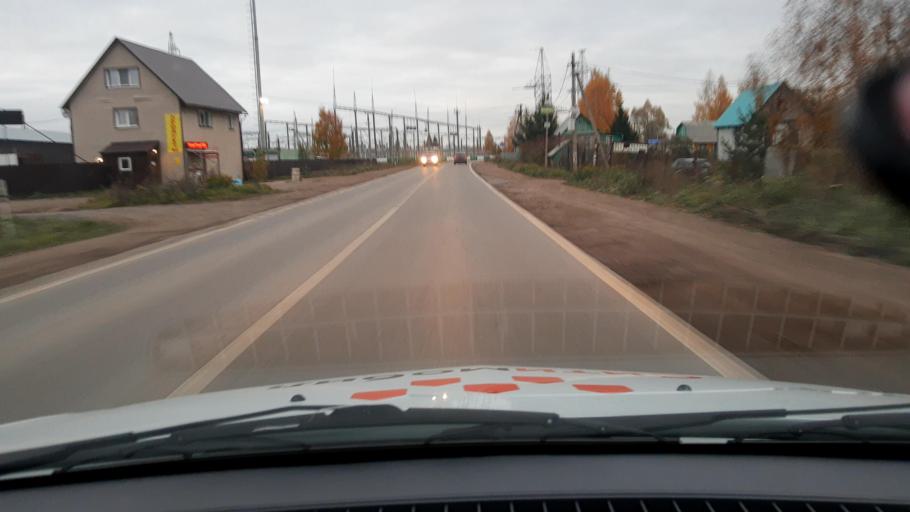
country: RU
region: Bashkortostan
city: Ufa
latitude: 54.6696
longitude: 56.0809
